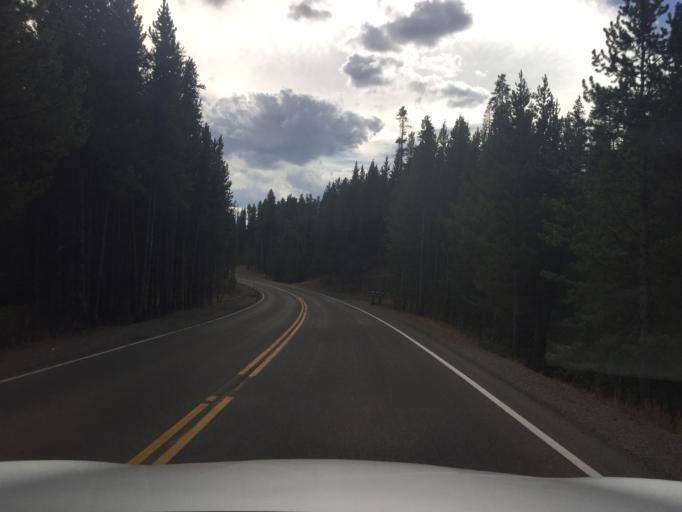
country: US
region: Montana
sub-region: Gallatin County
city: West Yellowstone
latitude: 44.7188
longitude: -110.5042
